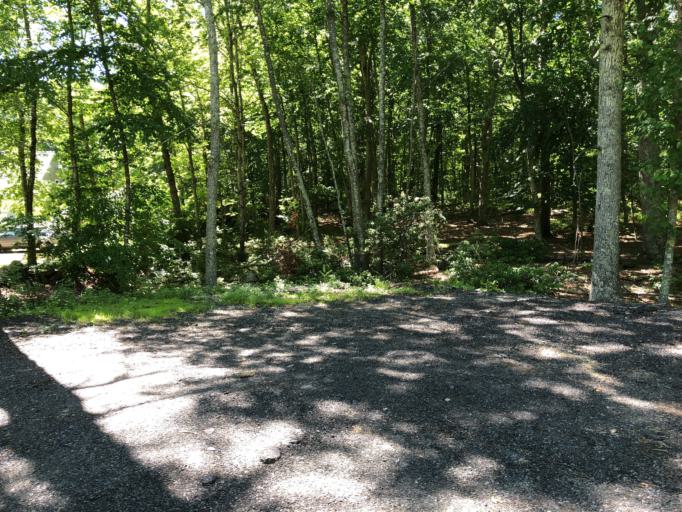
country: US
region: Rhode Island
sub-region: Washington County
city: Hopkinton
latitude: 41.5071
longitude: -71.8039
